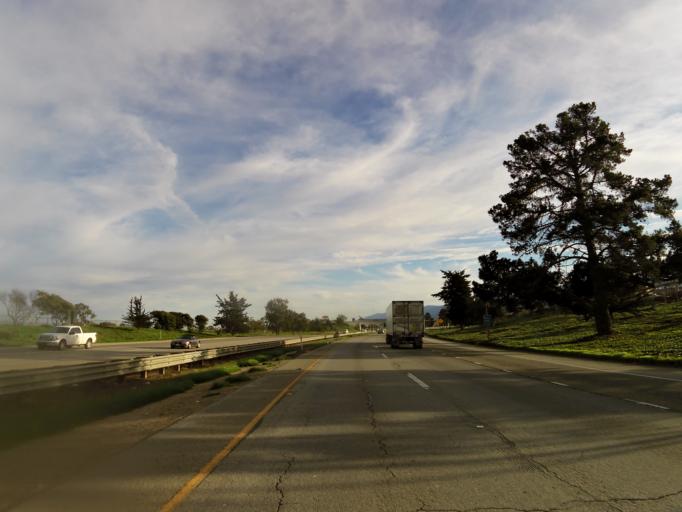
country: US
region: California
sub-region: Monterey County
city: Salinas
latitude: 36.6643
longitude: -121.6251
